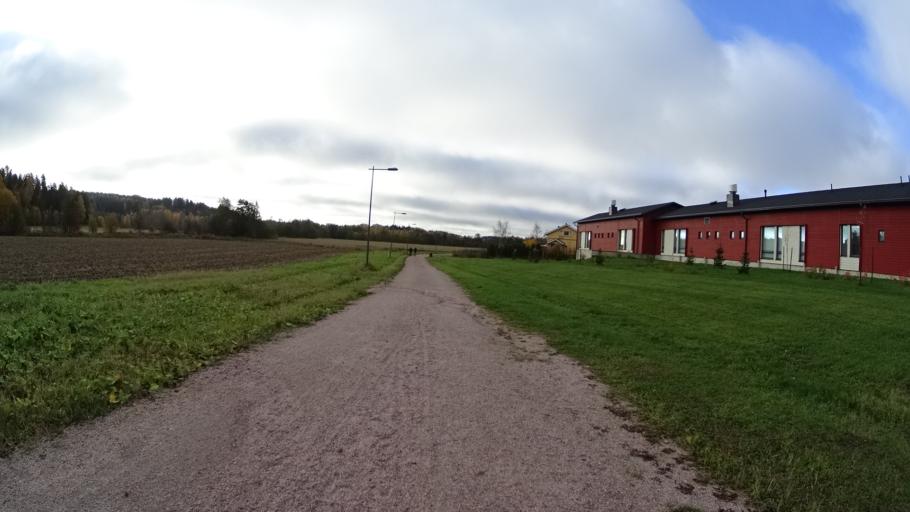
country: FI
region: Uusimaa
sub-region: Helsinki
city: Espoo
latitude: 60.2201
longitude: 24.6732
